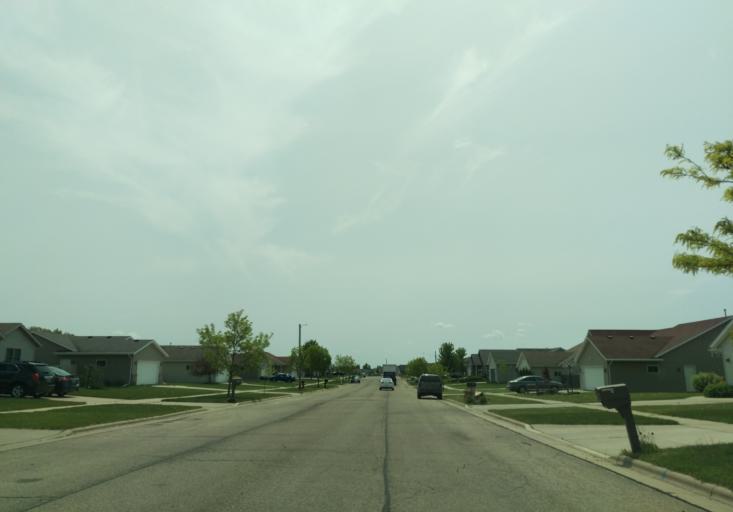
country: US
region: Wisconsin
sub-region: Rock County
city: Evansville
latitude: 42.7782
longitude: -89.3169
